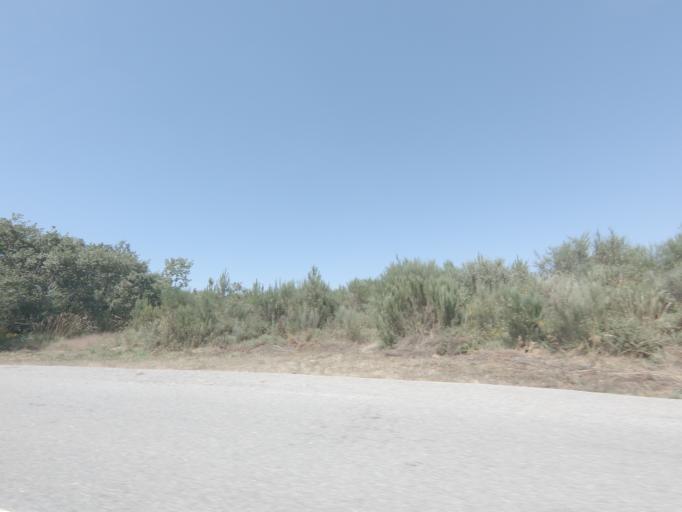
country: PT
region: Viseu
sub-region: Tarouca
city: Tarouca
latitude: 40.9908
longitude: -7.8355
